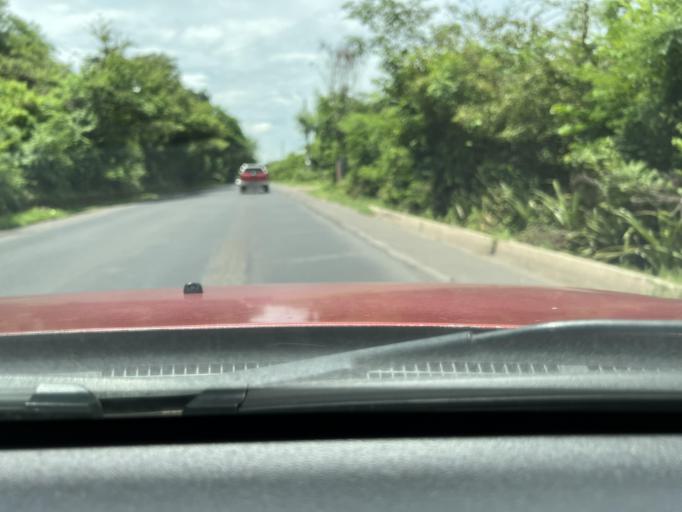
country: SV
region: Usulutan
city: Berlin
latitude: 13.6025
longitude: -88.5883
